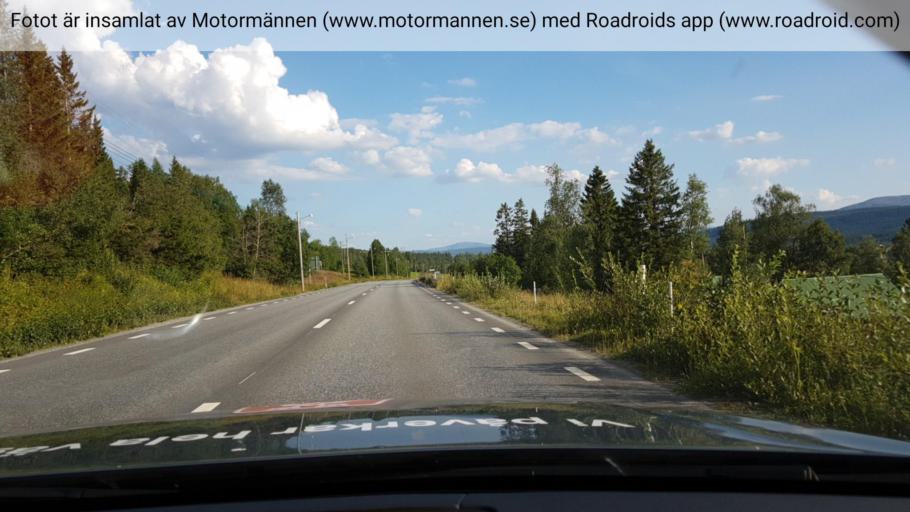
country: SE
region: Jaemtland
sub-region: Are Kommun
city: Are
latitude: 63.3582
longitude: 13.1814
